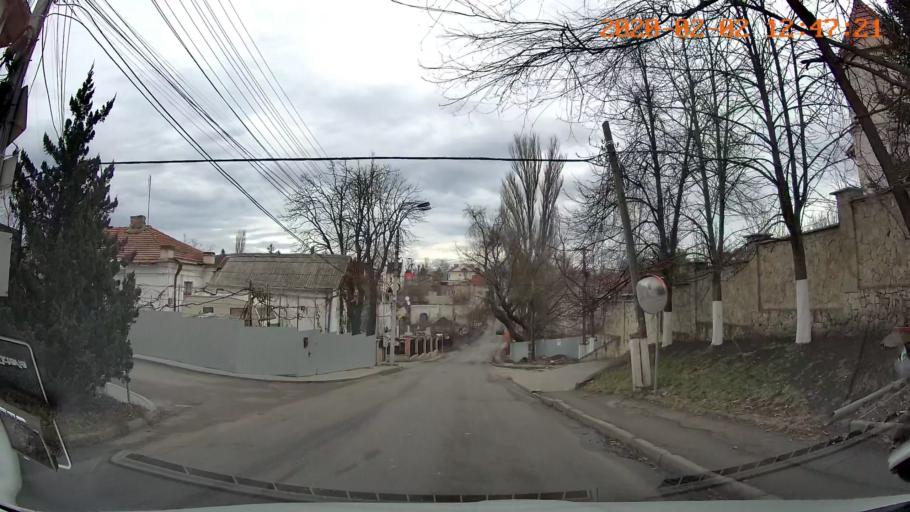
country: MD
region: Chisinau
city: Chisinau
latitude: 47.0124
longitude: 28.8240
